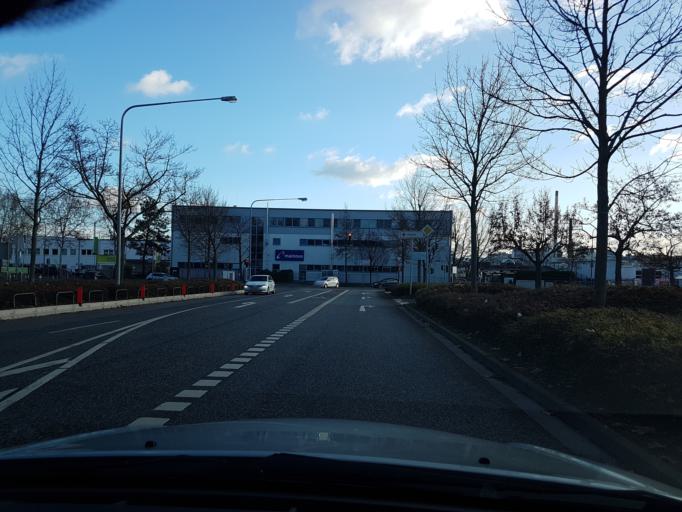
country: DE
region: Hesse
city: Sulzbach
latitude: 50.1021
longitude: 8.5297
